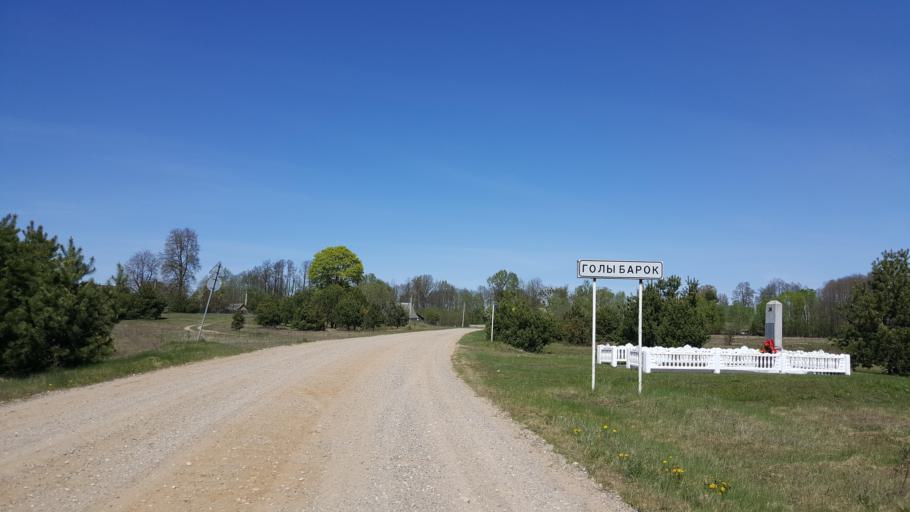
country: BY
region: Brest
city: Kamyanyets
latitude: 52.4229
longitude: 23.8432
